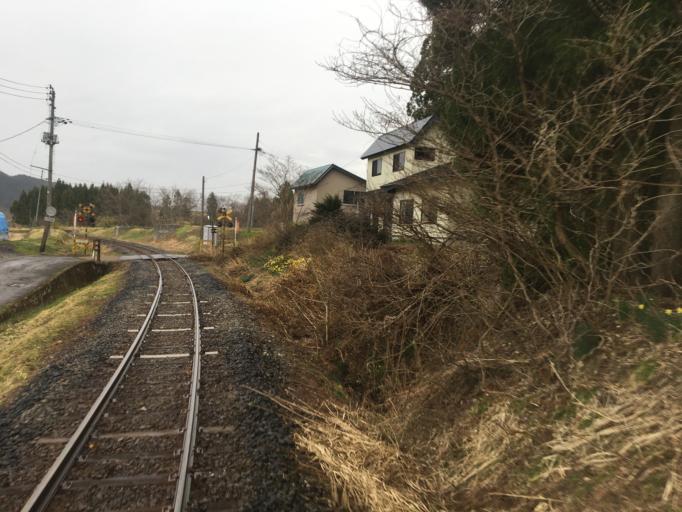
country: JP
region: Akita
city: Takanosu
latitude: 40.0399
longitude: 140.3999
